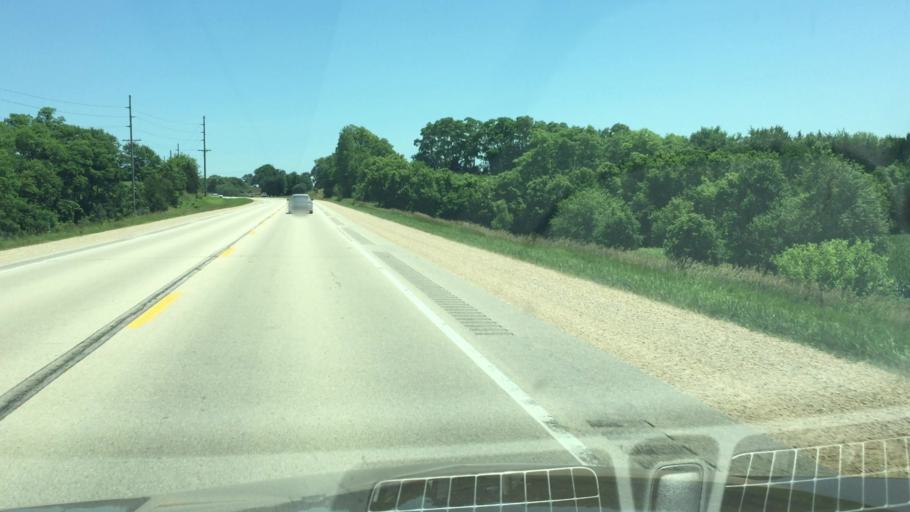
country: US
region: Iowa
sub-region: Jackson County
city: Maquoketa
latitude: 42.0630
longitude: -90.7606
